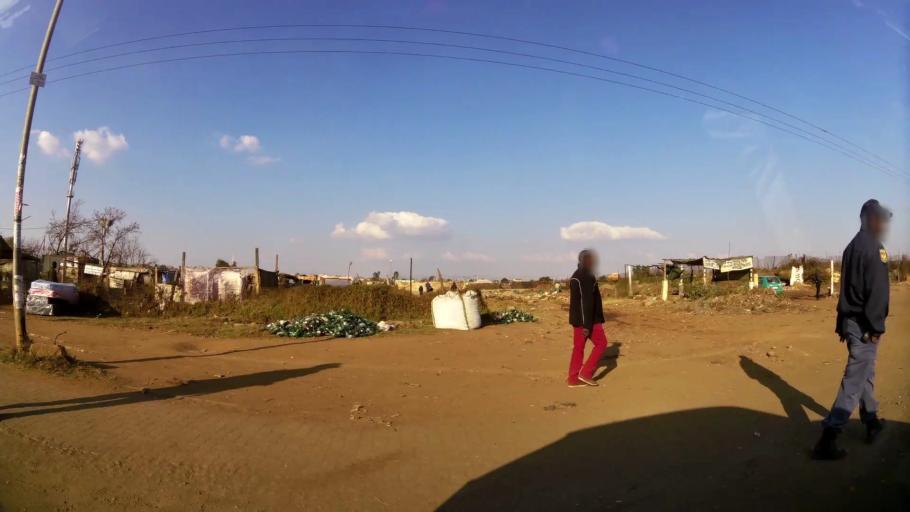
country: ZA
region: Gauteng
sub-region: Ekurhuleni Metropolitan Municipality
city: Tembisa
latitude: -25.9757
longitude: 28.2117
